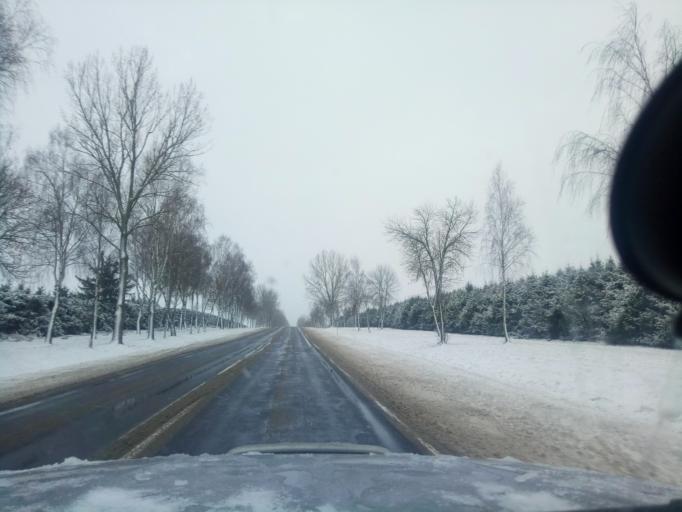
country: BY
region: Minsk
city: Haradzyeya
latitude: 53.3558
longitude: 26.5156
